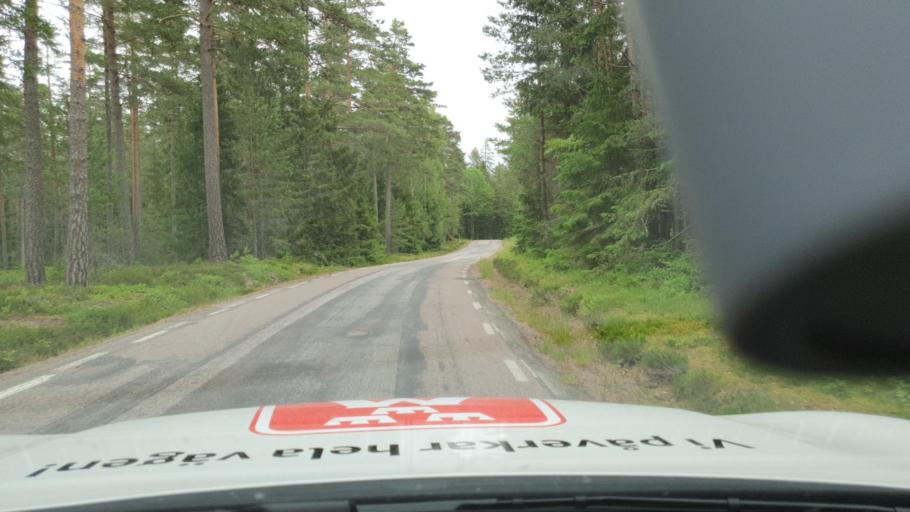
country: SE
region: Vaestra Goetaland
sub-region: Karlsborgs Kommun
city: Molltorp
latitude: 58.4173
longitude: 14.3363
